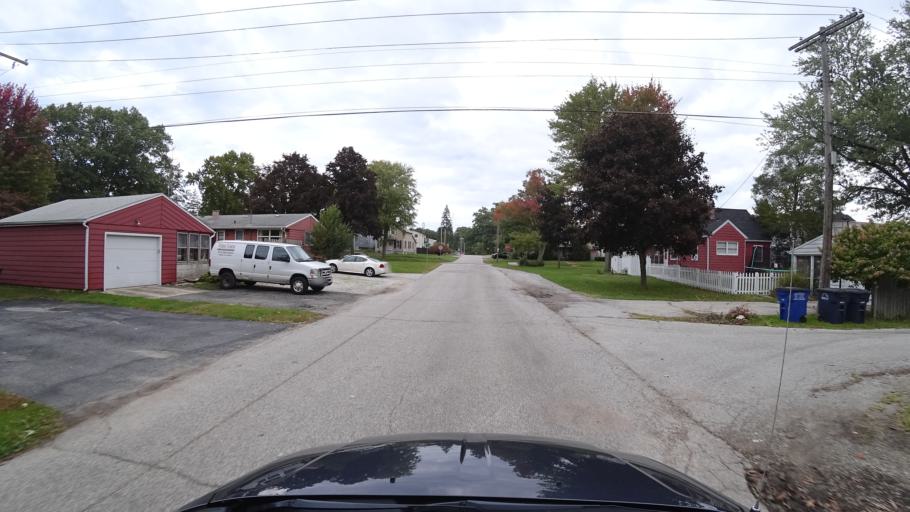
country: US
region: Indiana
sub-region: LaPorte County
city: Michigan City
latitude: 41.6980
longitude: -86.8891
